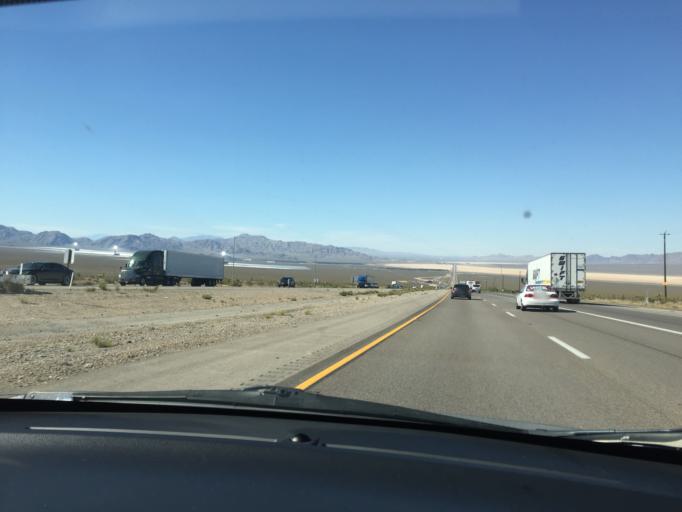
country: US
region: Nevada
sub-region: Clark County
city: Sandy Valley
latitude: 35.4754
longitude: -115.4476
